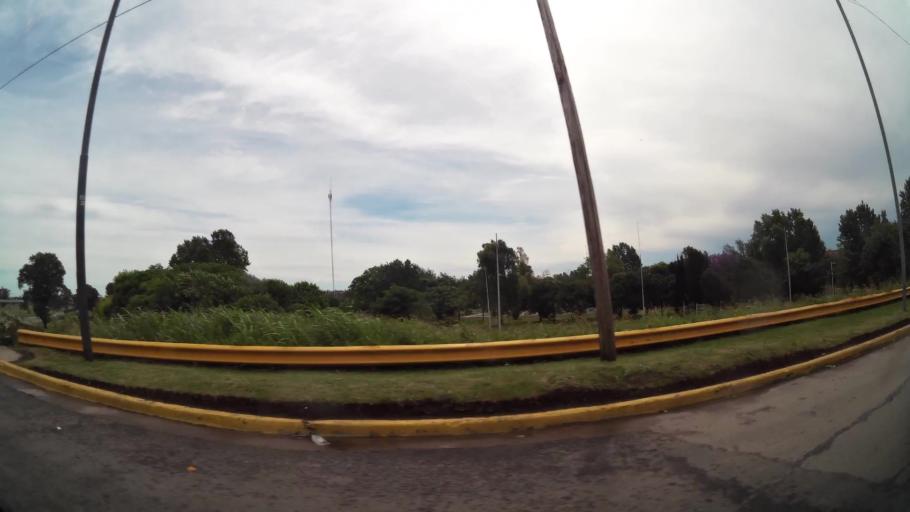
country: AR
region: Buenos Aires F.D.
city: Villa Lugano
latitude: -34.6668
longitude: -58.4522
